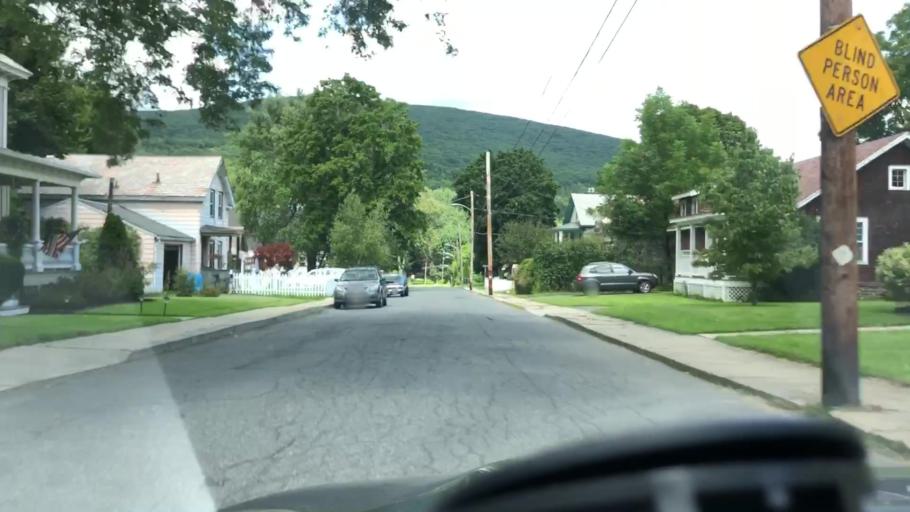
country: US
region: Massachusetts
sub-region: Berkshire County
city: North Adams
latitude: 42.6967
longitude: -73.1347
